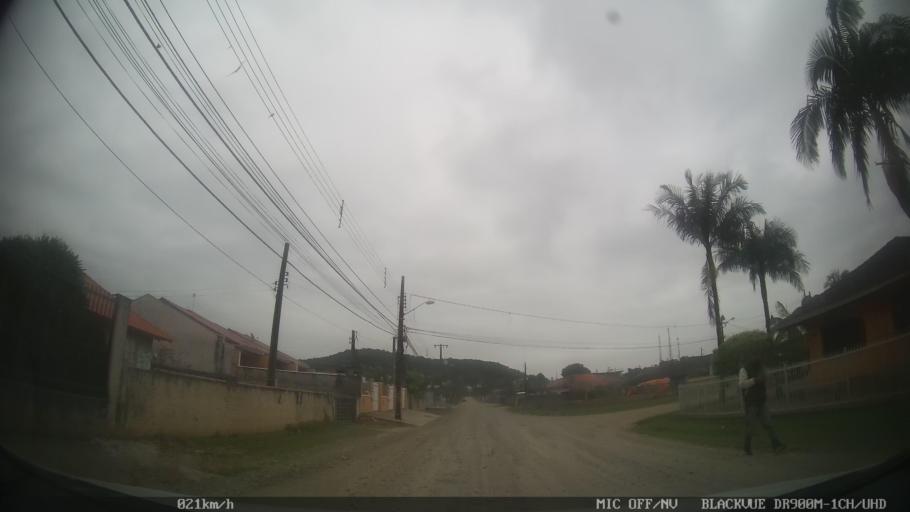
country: BR
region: Santa Catarina
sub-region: Joinville
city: Joinville
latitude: -26.3694
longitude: -48.8284
